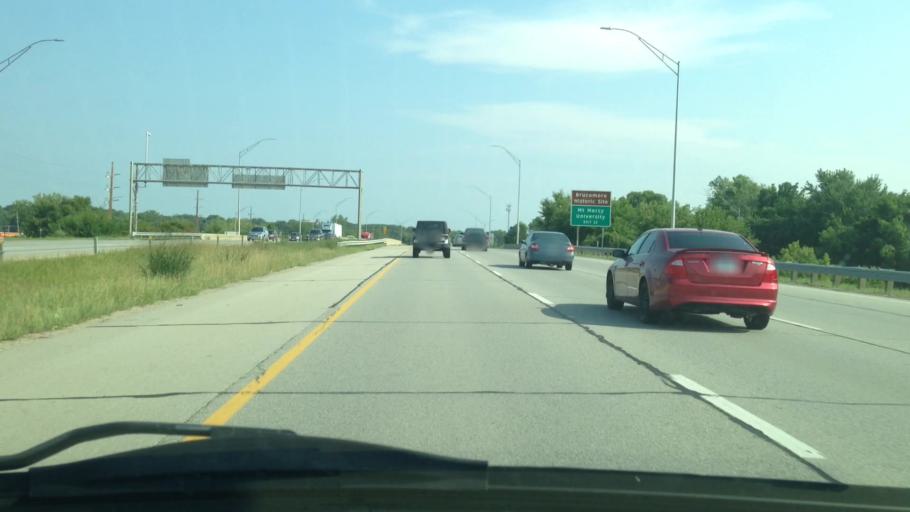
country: US
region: Iowa
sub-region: Linn County
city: Hiawatha
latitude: 42.0227
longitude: -91.6695
